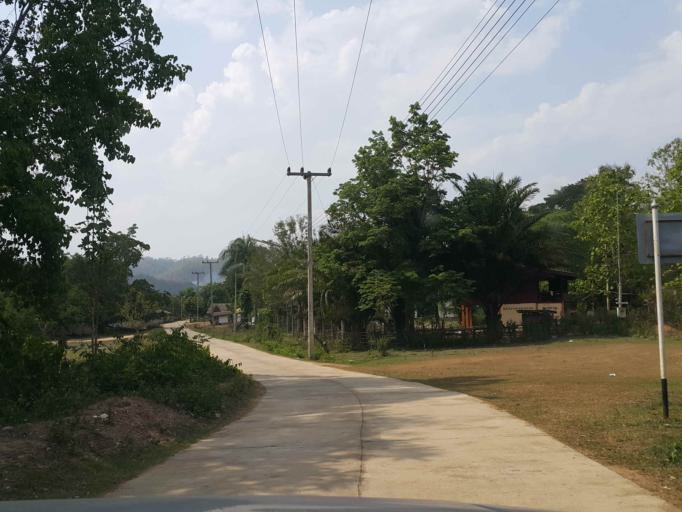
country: TH
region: Chiang Mai
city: Wiang Haeng
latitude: 19.3915
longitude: 98.7225
